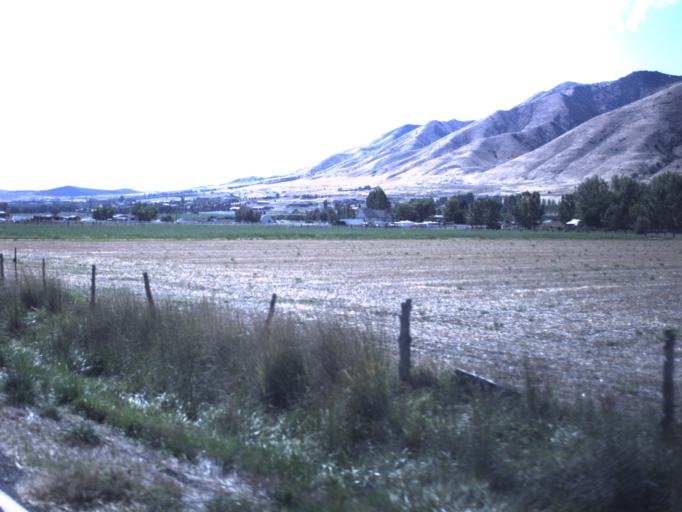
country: US
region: Utah
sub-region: Utah County
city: West Mountain
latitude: 40.0815
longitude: -111.7879
